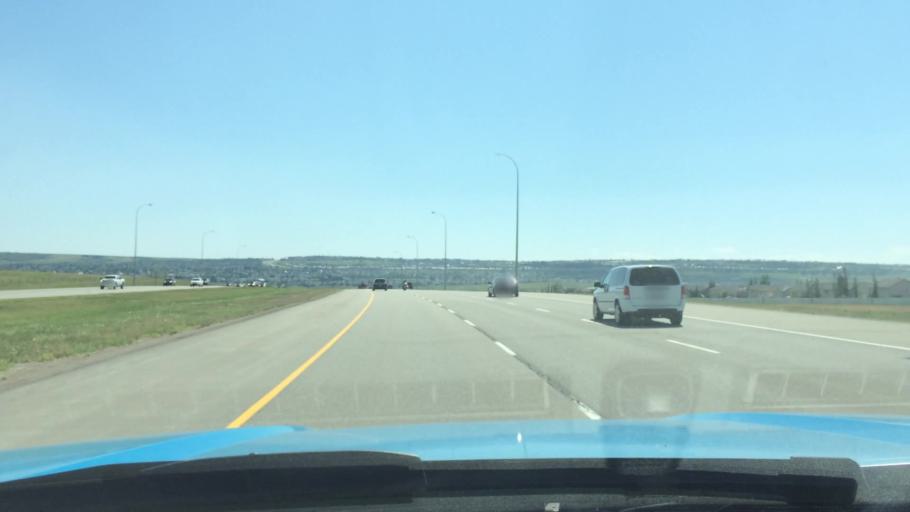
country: CA
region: Alberta
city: Calgary
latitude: 51.1685
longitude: -114.1051
